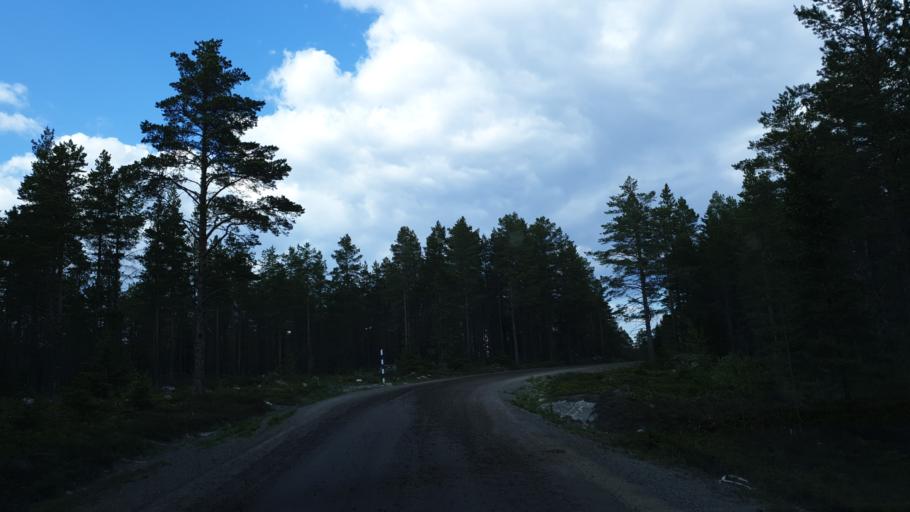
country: SE
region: Vaesterbotten
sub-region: Robertsfors Kommun
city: Robertsfors
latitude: 64.0080
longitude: 20.8947
